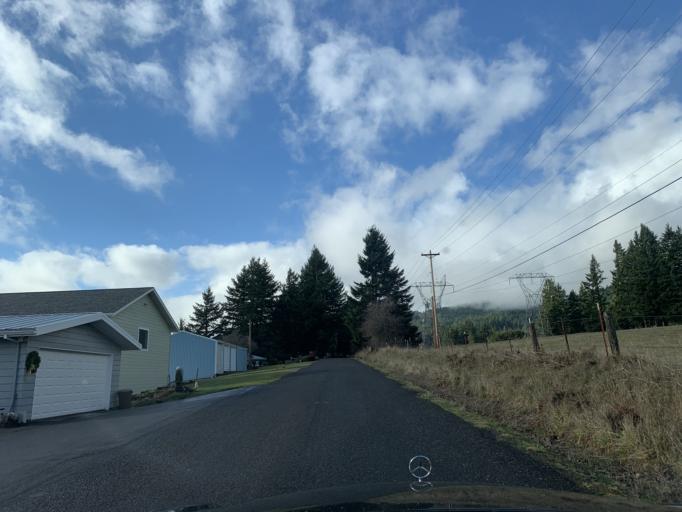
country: US
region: Washington
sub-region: Skamania County
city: Carson
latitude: 45.7223
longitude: -121.8105
